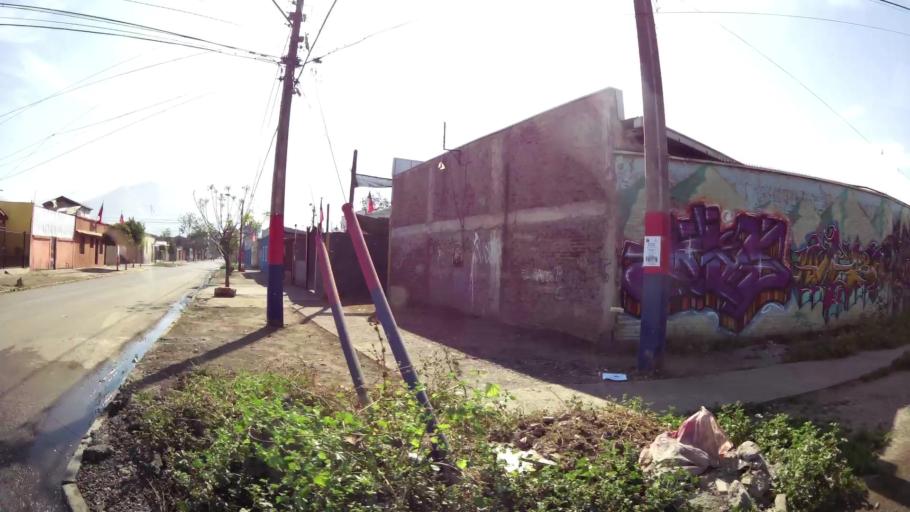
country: CL
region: Santiago Metropolitan
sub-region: Provincia de Santiago
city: Santiago
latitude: -33.3971
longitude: -70.6293
